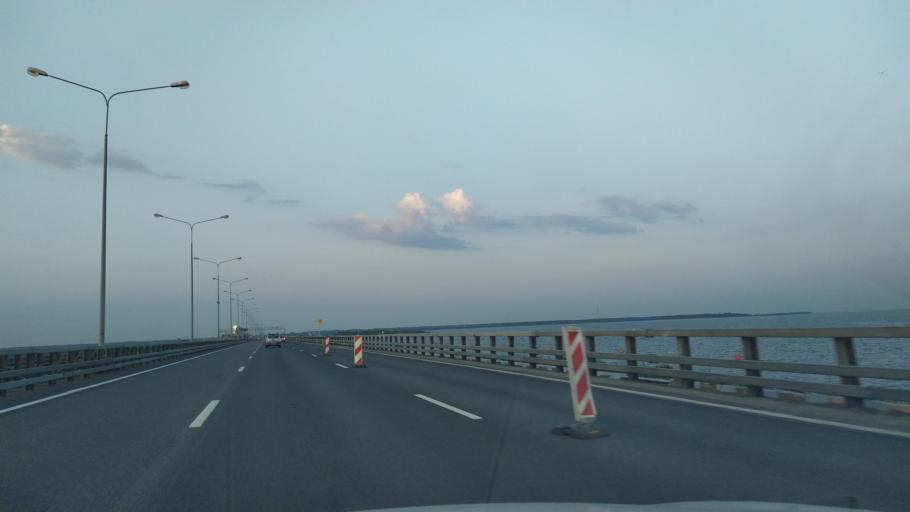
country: RU
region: Leningrad
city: Gorskaya
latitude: 60.0309
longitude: 29.8915
